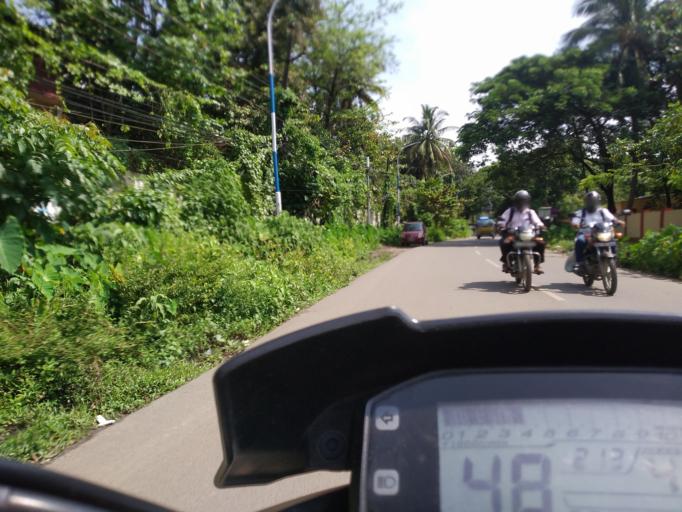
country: IN
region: Kerala
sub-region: Ernakulam
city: Cochin
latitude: 9.9679
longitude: 76.2926
